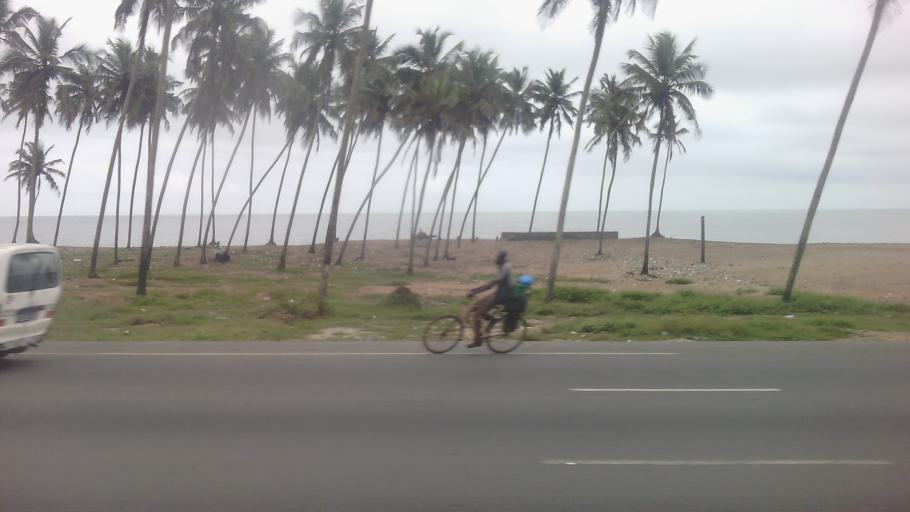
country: CI
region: Lagunes
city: Abidjan
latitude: 5.2459
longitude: -3.9377
